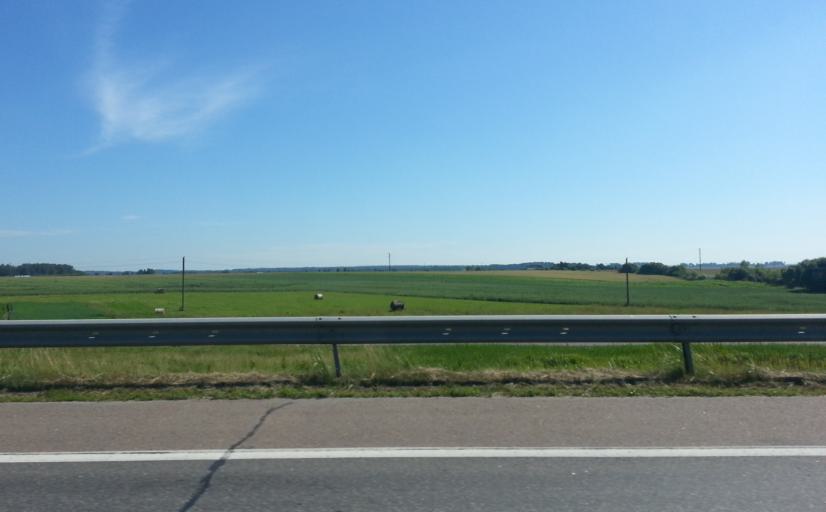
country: LT
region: Vilnius County
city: Ukmerge
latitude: 55.3140
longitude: 24.7829
